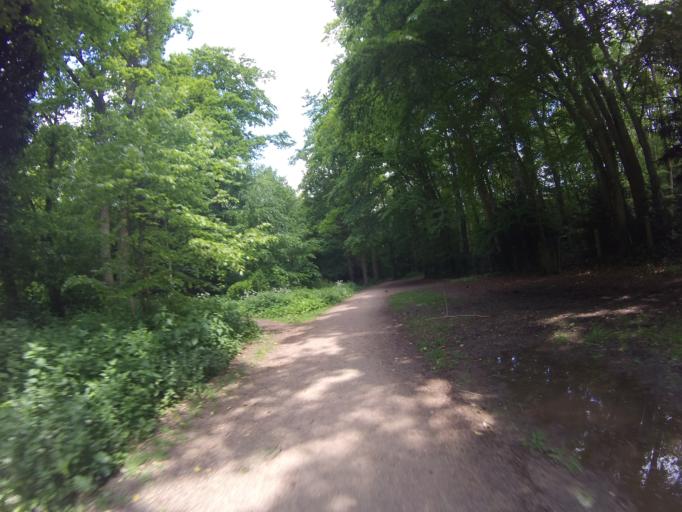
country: NL
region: North Holland
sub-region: Gemeente Laren
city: Laren
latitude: 52.2592
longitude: 5.2389
